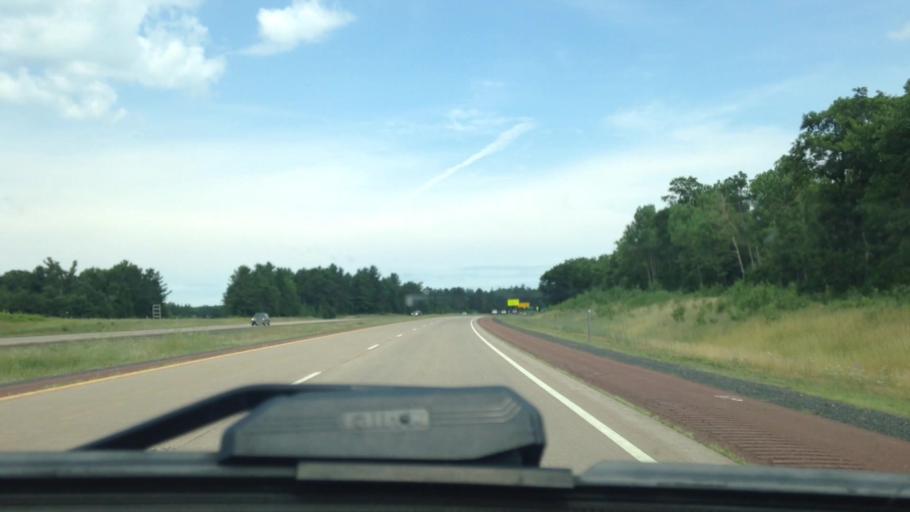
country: US
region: Wisconsin
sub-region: Douglas County
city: Lake Nebagamon
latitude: 46.3387
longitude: -91.8315
